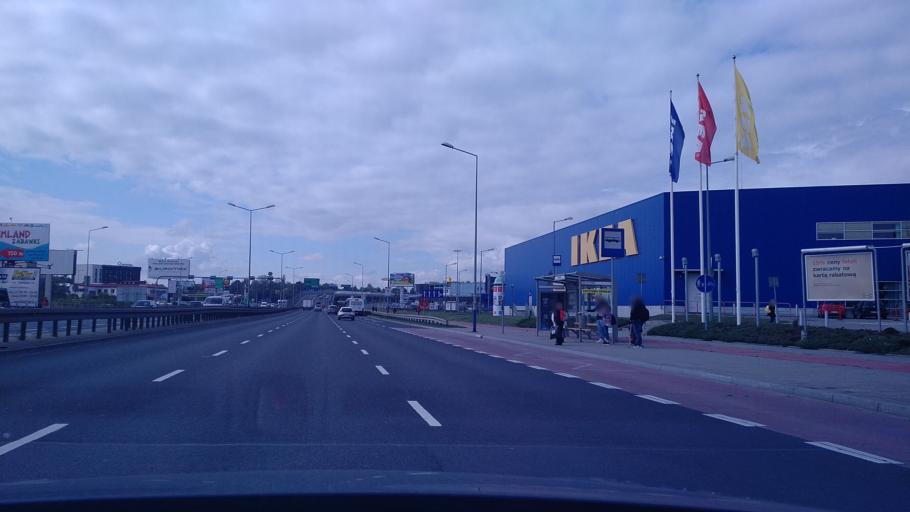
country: PL
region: Lesser Poland Voivodeship
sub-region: Powiat krakowski
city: Zielonki
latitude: 50.0885
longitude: 19.8987
